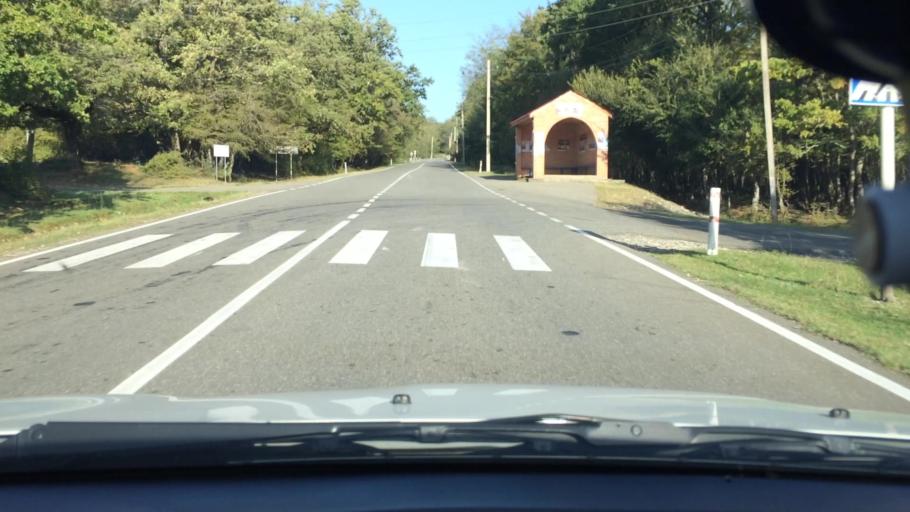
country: GE
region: Imereti
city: Kutaisi
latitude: 42.2457
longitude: 42.7588
